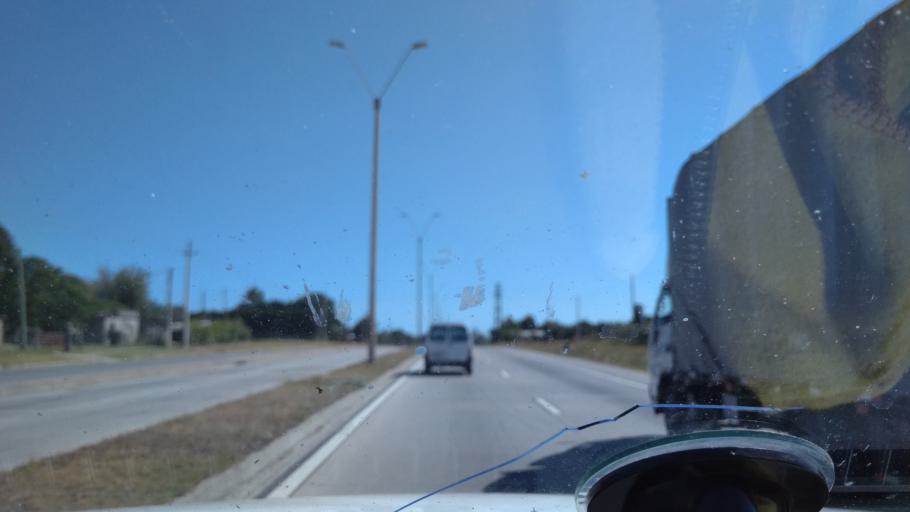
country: UY
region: Canelones
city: Toledo
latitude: -34.7913
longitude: -56.1123
